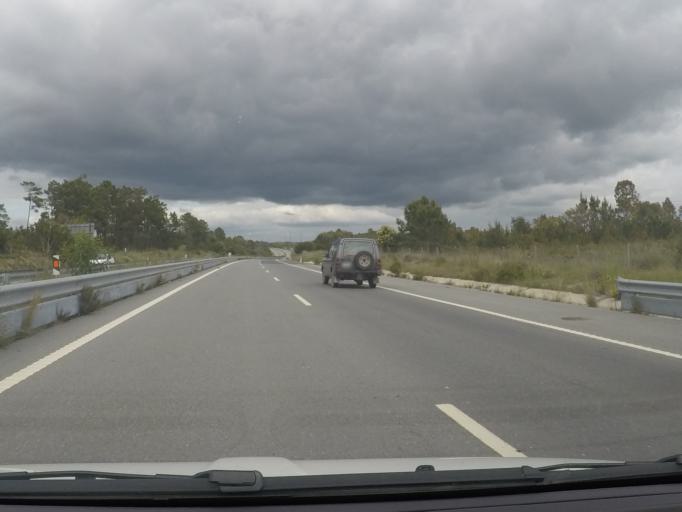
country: PT
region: Setubal
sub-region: Santiago do Cacem
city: Santo Andre
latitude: 37.9856
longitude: -8.7815
